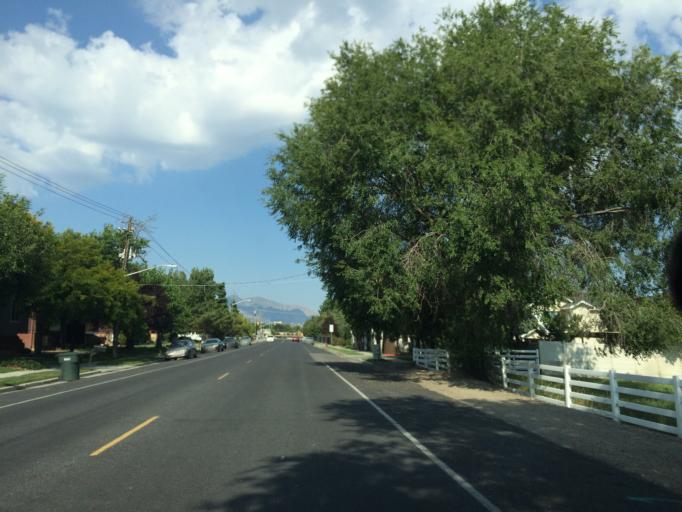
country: US
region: Utah
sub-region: Salt Lake County
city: West Valley City
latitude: 40.6929
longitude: -111.9740
